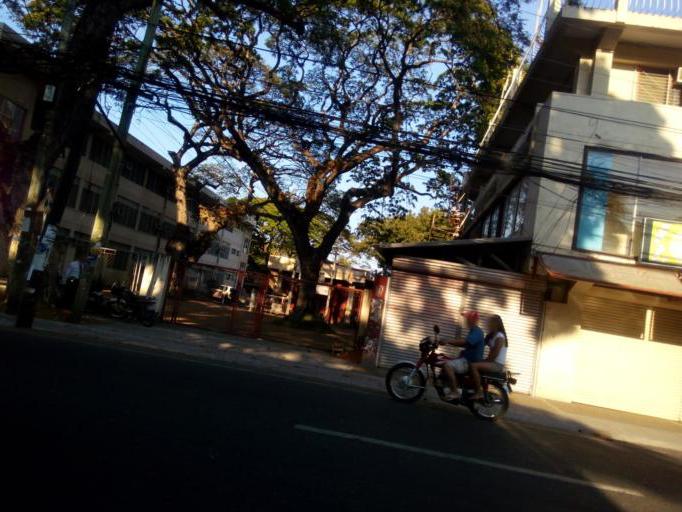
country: PH
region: Central Visayas
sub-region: Province of Negros Oriental
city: Dumaguete
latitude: 9.3122
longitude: 123.3074
